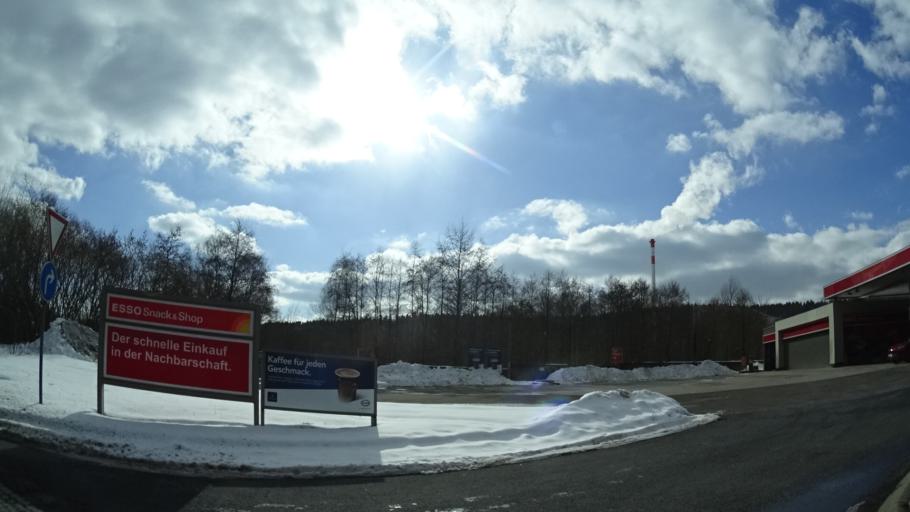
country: DE
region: Thuringia
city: Suhl
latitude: 50.6412
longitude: 10.6912
